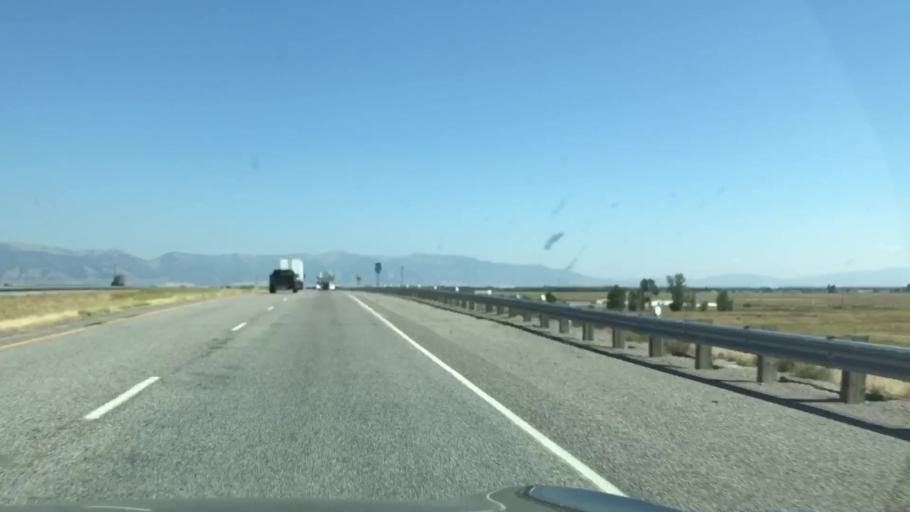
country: US
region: Montana
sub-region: Gallatin County
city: Manhattan
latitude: 45.8488
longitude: -111.3294
